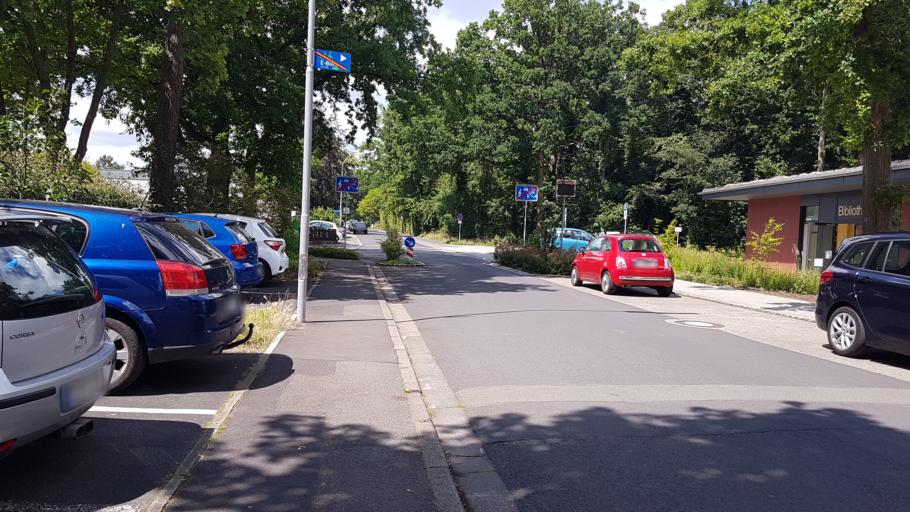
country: DE
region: Bavaria
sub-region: Regierungsbezirk Unterfranken
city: Schwebheim
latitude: 49.9987
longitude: 10.2503
